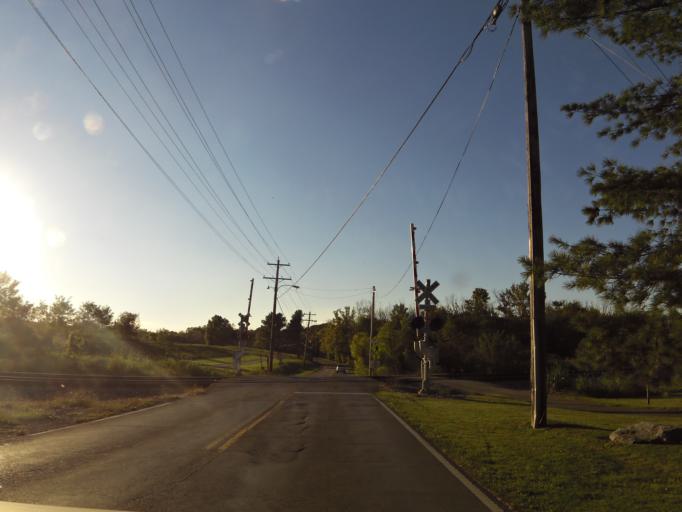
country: US
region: Tennessee
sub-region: Blount County
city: Alcoa
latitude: 35.7922
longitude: -83.9642
